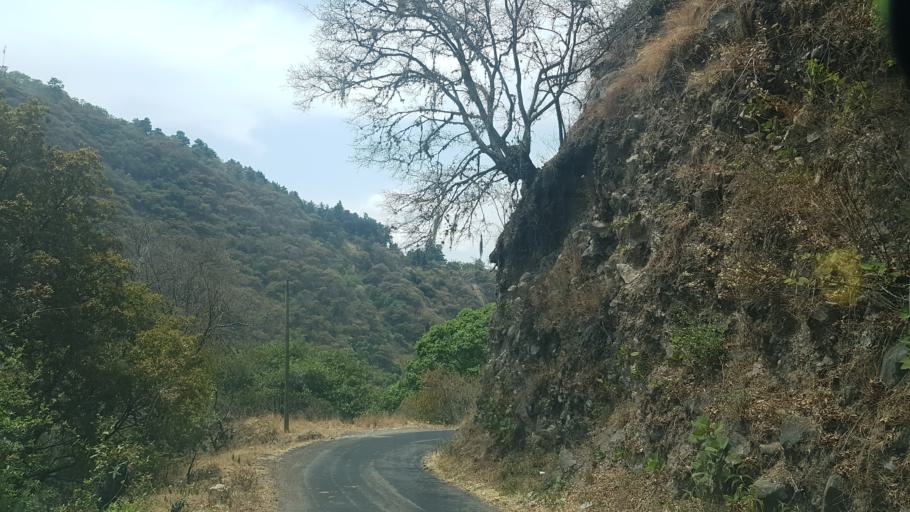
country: MX
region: Puebla
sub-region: Tochimilco
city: La Magdalena Yancuitlalpan
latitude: 18.8738
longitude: -98.6043
